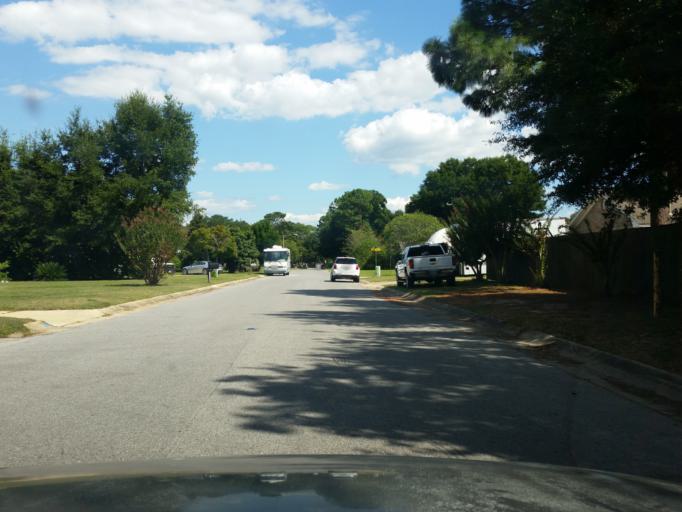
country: US
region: Florida
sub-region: Escambia County
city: Ferry Pass
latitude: 30.5149
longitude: -87.1848
